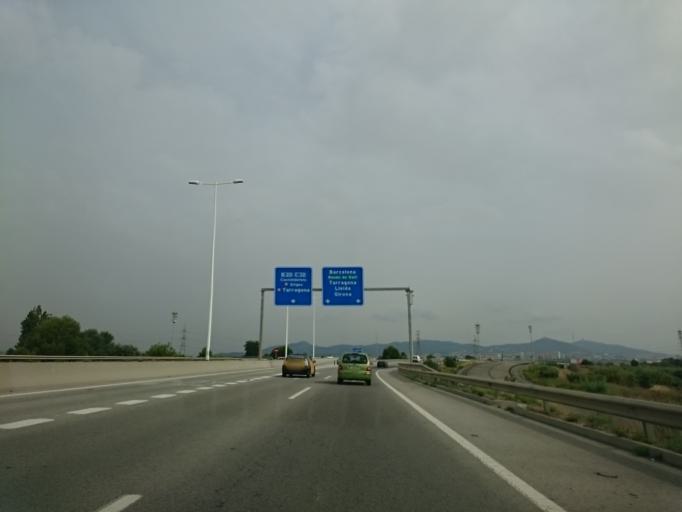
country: ES
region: Catalonia
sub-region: Provincia de Barcelona
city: Cornella de Llobregat
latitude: 41.3301
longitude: 2.0706
